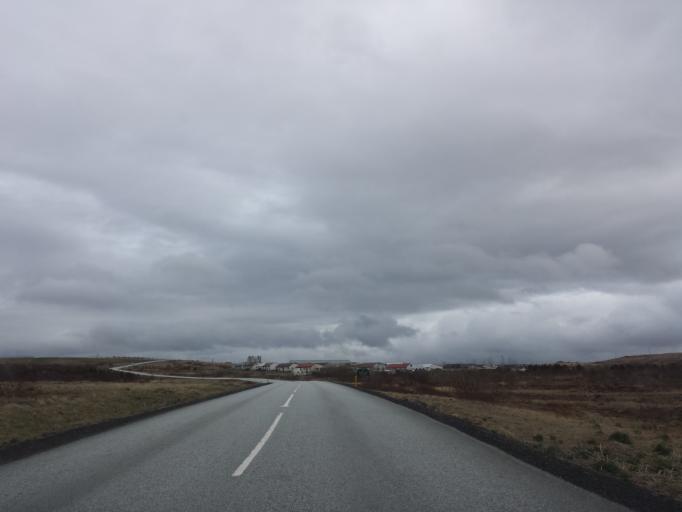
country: IS
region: Capital Region
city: Kopavogur
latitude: 64.0778
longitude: -21.8534
